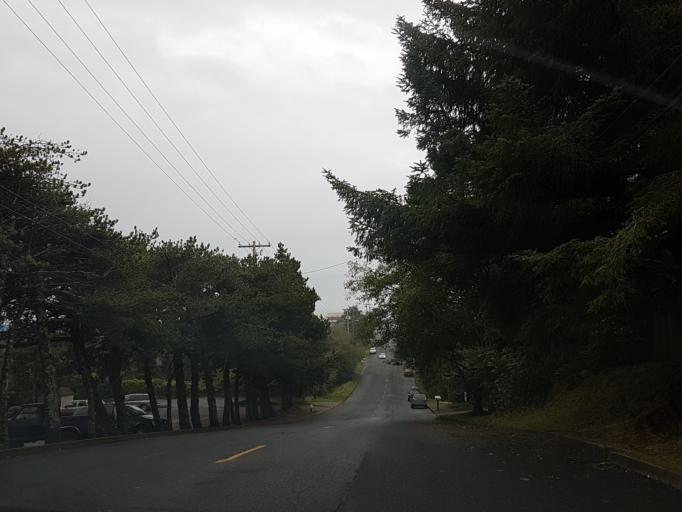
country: US
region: Oregon
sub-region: Lincoln County
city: Newport
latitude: 44.6401
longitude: -124.0557
